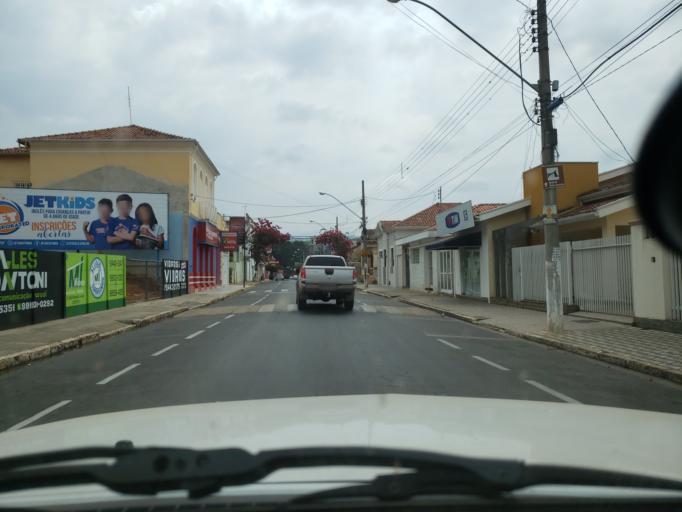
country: BR
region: Minas Gerais
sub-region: Jacutinga
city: Jacutinga
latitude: -22.2849
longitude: -46.6119
